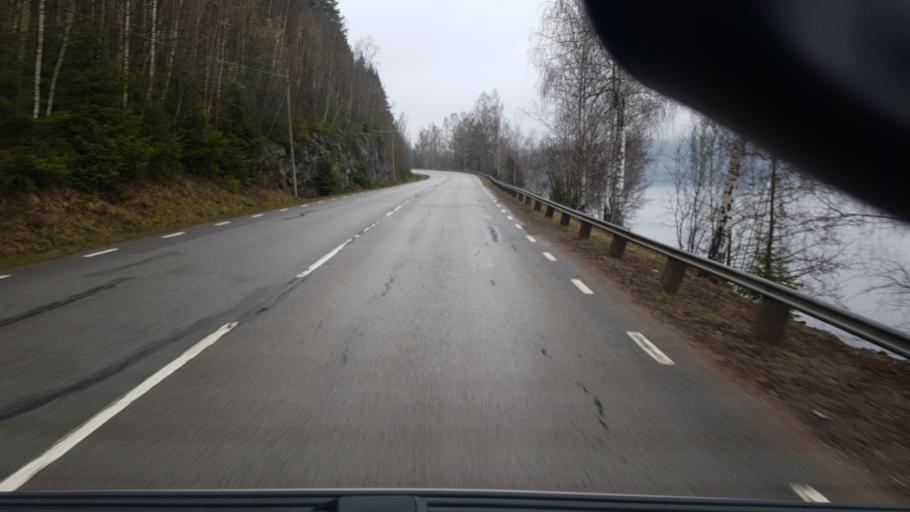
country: SE
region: Vaermland
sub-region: Arvika Kommun
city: Arvika
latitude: 59.7070
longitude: 12.6355
